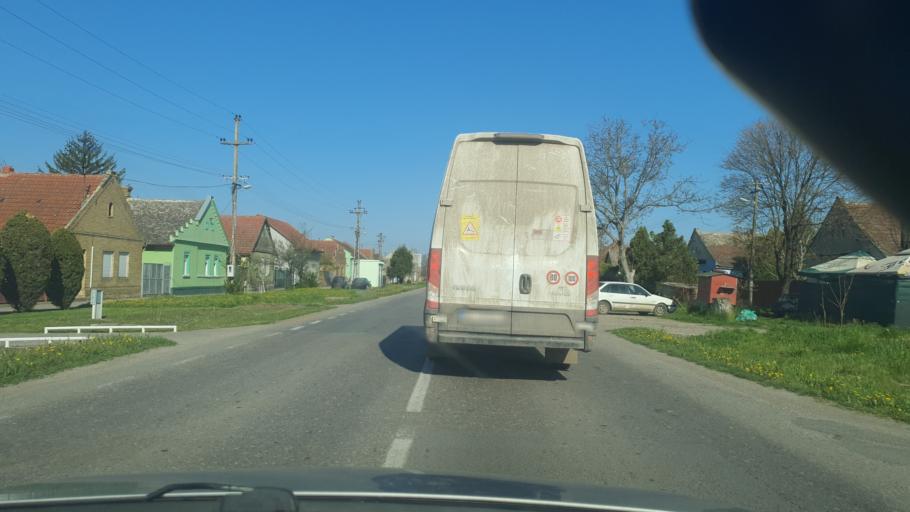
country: RS
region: Autonomna Pokrajina Vojvodina
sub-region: Zapadnobacki Okrug
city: Kula
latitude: 45.6642
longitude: 19.4438
